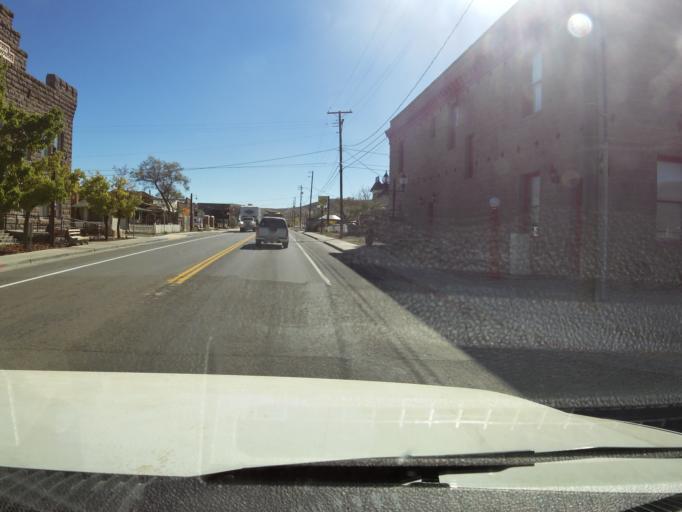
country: US
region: Nevada
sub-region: Esmeralda County
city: Goldfield
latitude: 37.7077
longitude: -117.2339
